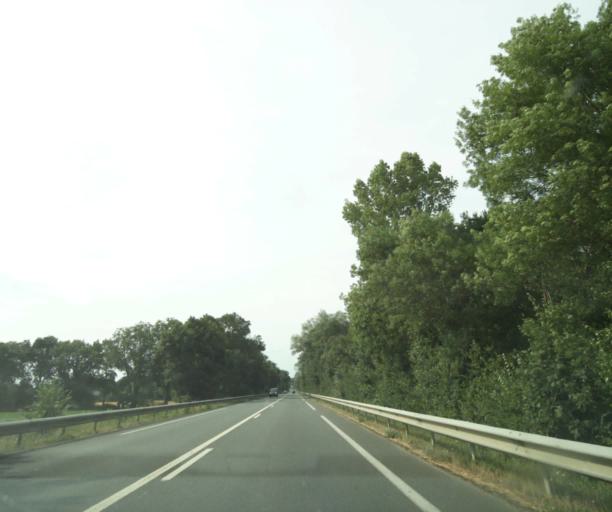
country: FR
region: Pays de la Loire
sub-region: Departement de la Sarthe
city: Chateau-du-Loir
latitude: 47.6784
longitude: 0.4485
